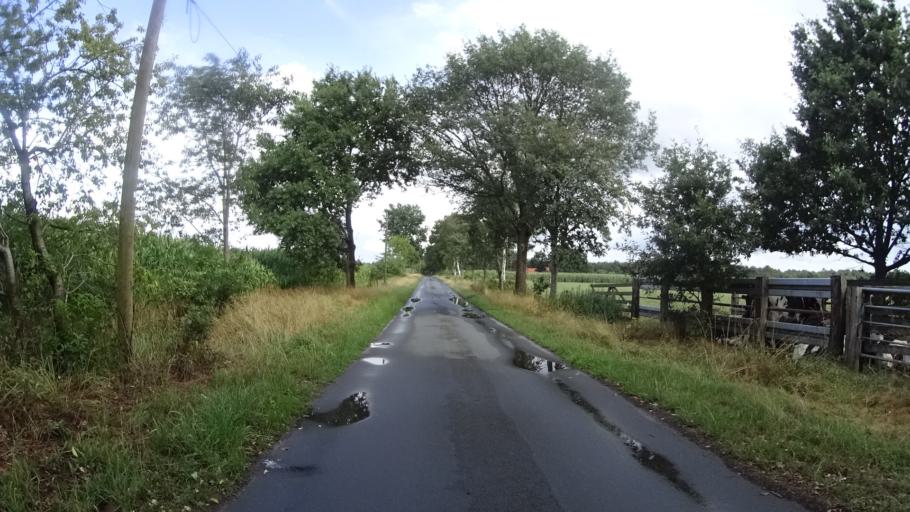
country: DE
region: Lower Saxony
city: Friedeburg
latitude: 53.3836
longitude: 7.8689
